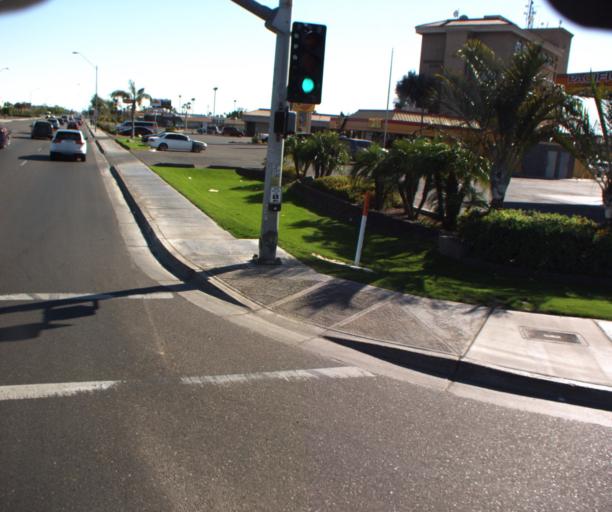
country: US
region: Arizona
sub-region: Yuma County
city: Yuma
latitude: 32.6838
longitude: -114.6247
